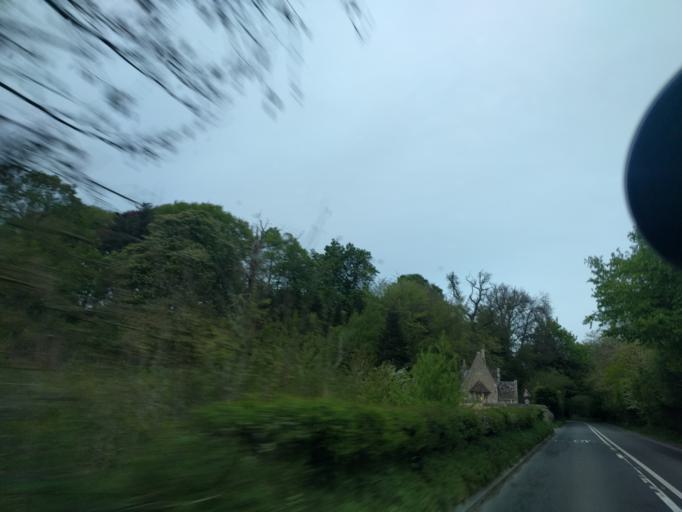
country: GB
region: England
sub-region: Wiltshire
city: Devizes
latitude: 51.3374
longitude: -1.9981
